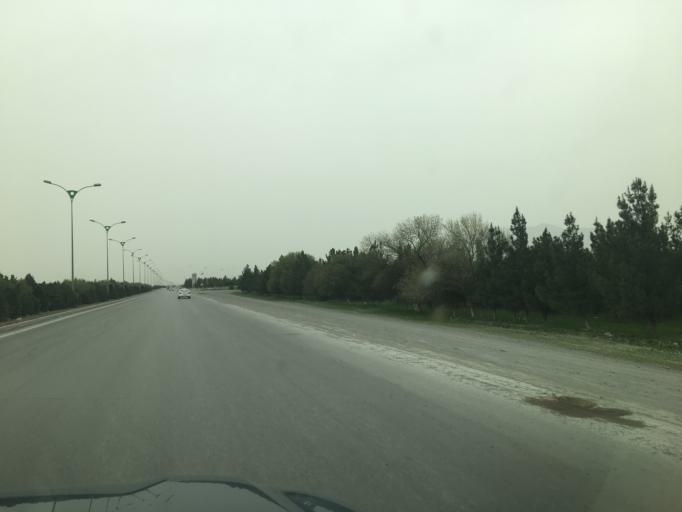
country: TM
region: Ahal
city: Abadan
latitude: 38.1466
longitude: 57.9889
